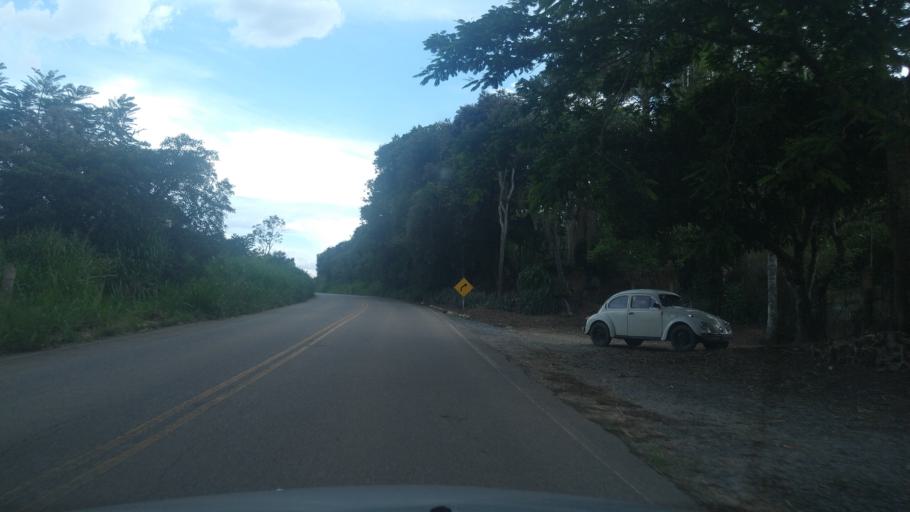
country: BR
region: Minas Gerais
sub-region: Extrema
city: Extrema
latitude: -22.7914
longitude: -46.3185
